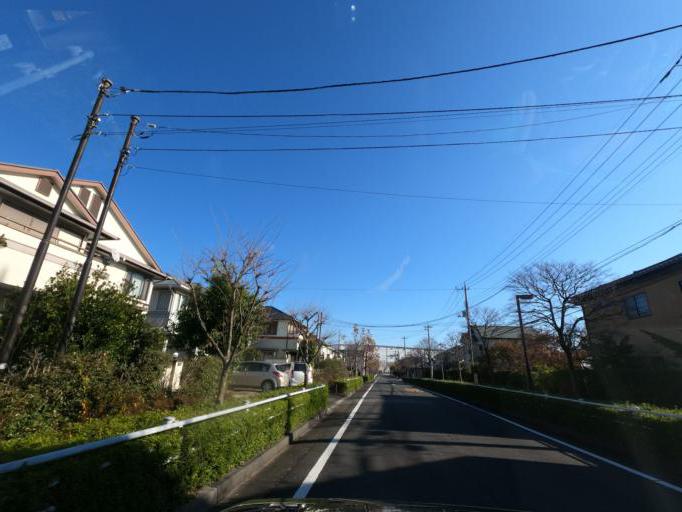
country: JP
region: Ibaraki
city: Mitsukaido
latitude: 35.9729
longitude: 139.9759
